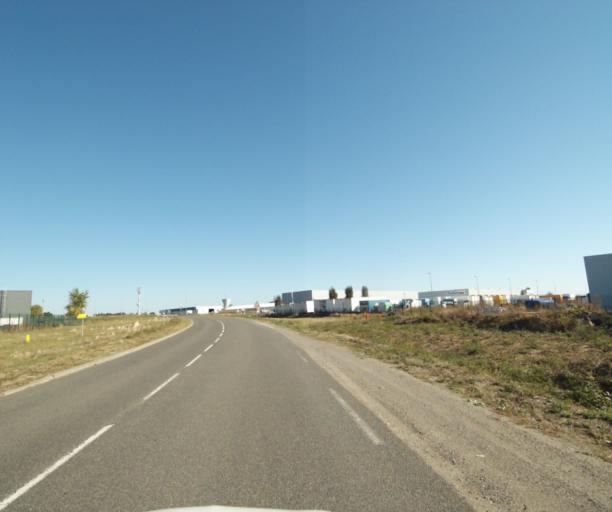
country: FR
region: Auvergne
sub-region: Departement du Puy-de-Dome
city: Gerzat
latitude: 45.8327
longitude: 3.1380
